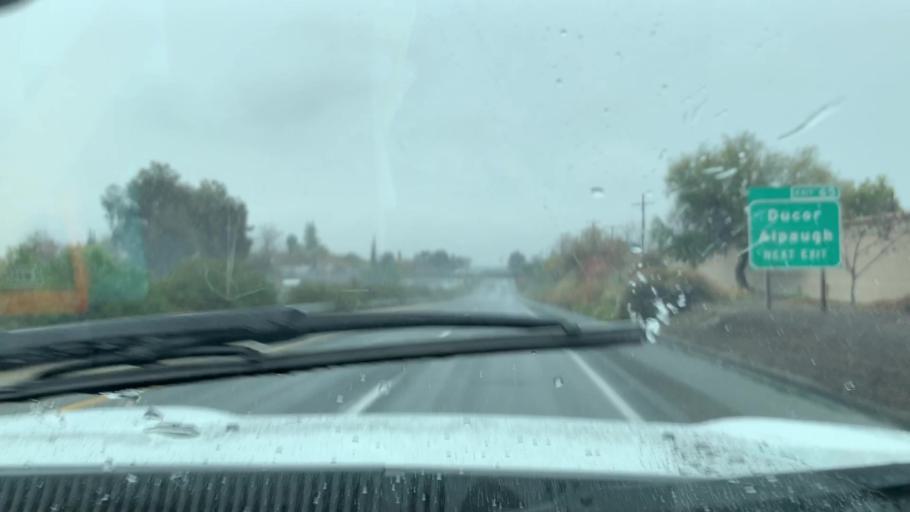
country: US
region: California
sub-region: Tulare County
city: Earlimart
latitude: 35.8820
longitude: -119.2714
